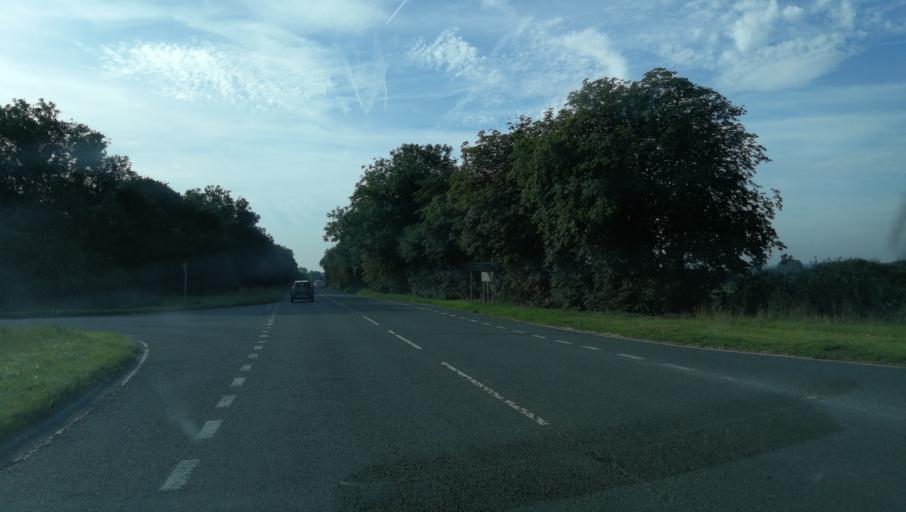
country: GB
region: England
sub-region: Oxfordshire
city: Woodstock
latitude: 51.8630
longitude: -1.3238
